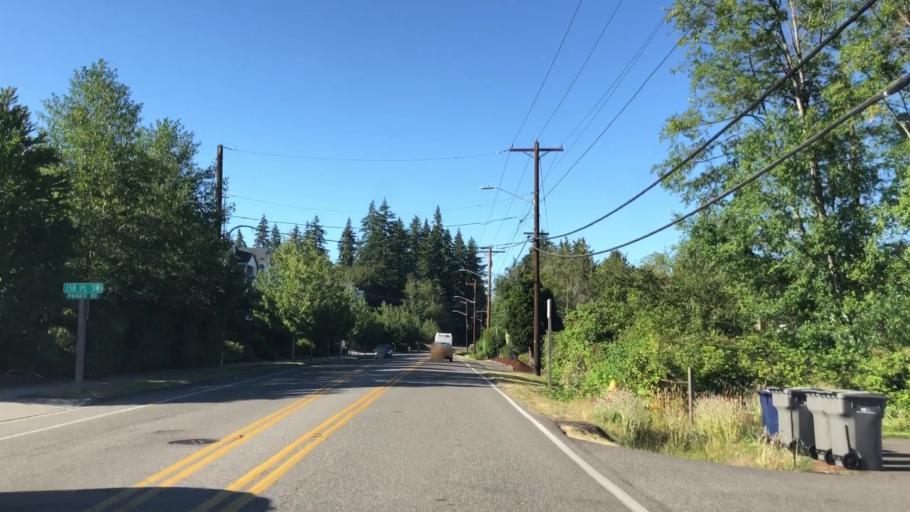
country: US
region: Washington
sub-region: Snohomish County
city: Martha Lake
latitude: 47.8549
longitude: -122.2721
